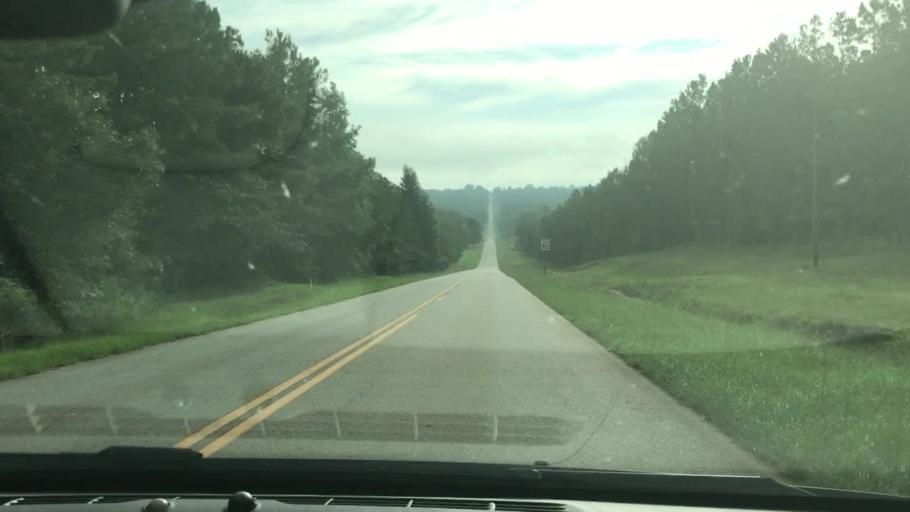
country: US
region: Georgia
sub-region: Quitman County
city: Georgetown
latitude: 31.9756
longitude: -84.9705
